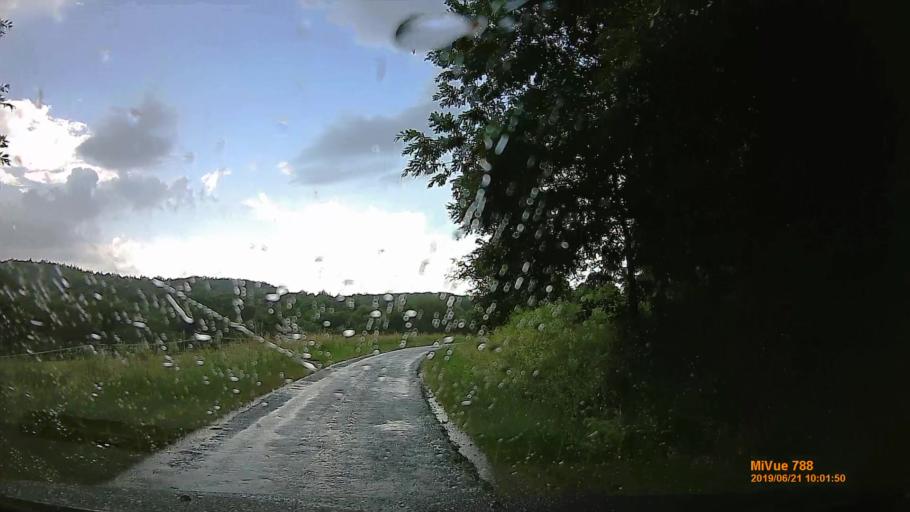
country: HU
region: Baranya
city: Buekkoesd
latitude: 46.2016
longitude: 17.9748
